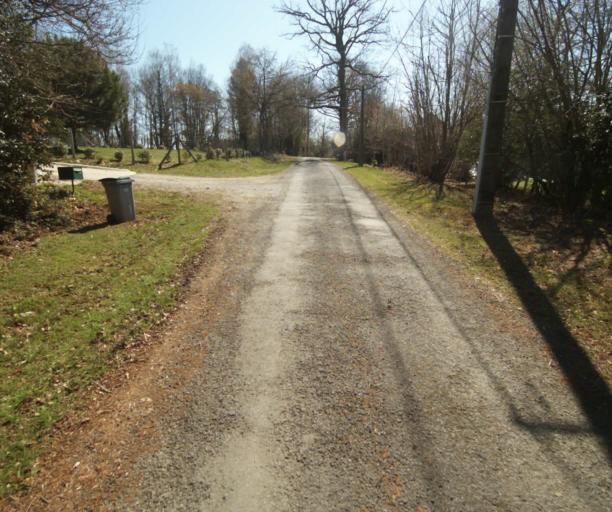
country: FR
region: Limousin
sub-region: Departement de la Correze
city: Saint-Clement
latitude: 45.3250
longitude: 1.6519
